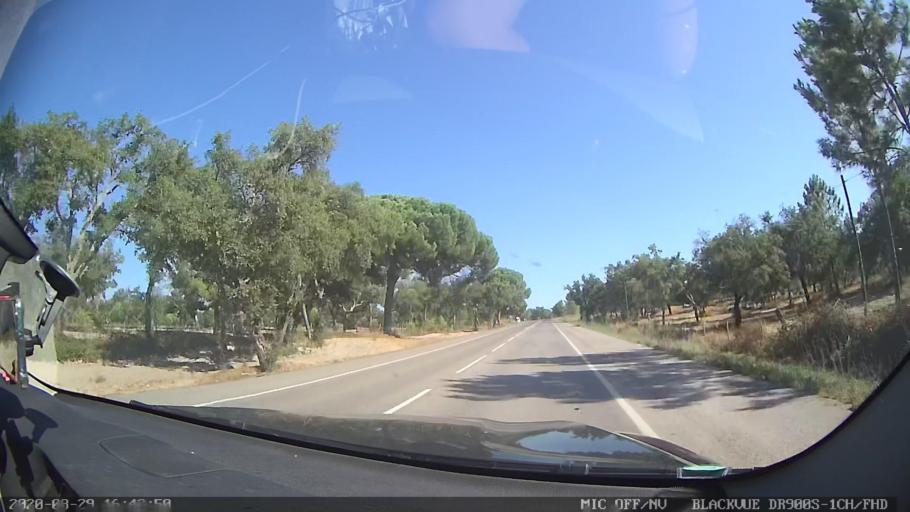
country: PT
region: Setubal
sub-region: Alcacer do Sal
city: Alcacer do Sal
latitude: 38.5416
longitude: -8.6441
